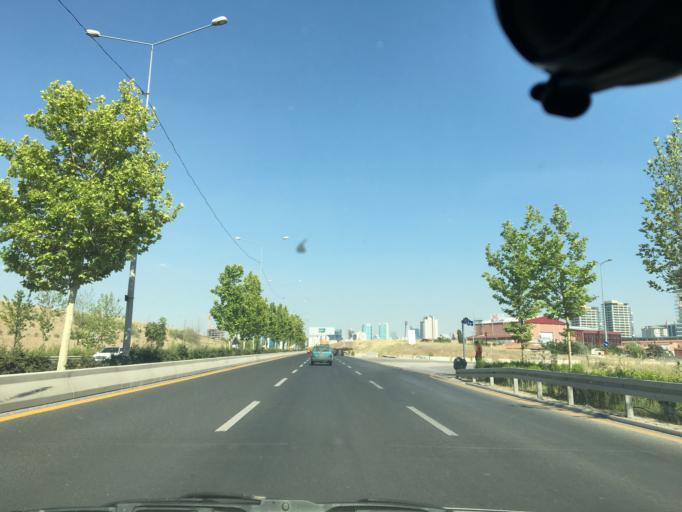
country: TR
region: Ankara
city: Batikent
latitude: 39.9168
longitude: 32.7713
